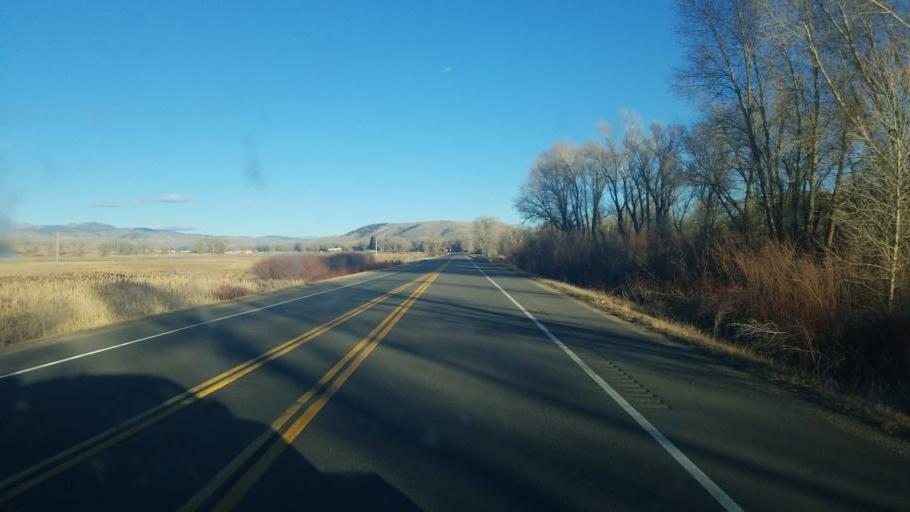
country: US
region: Colorado
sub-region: Gunnison County
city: Gunnison
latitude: 38.5227
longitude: -106.9861
